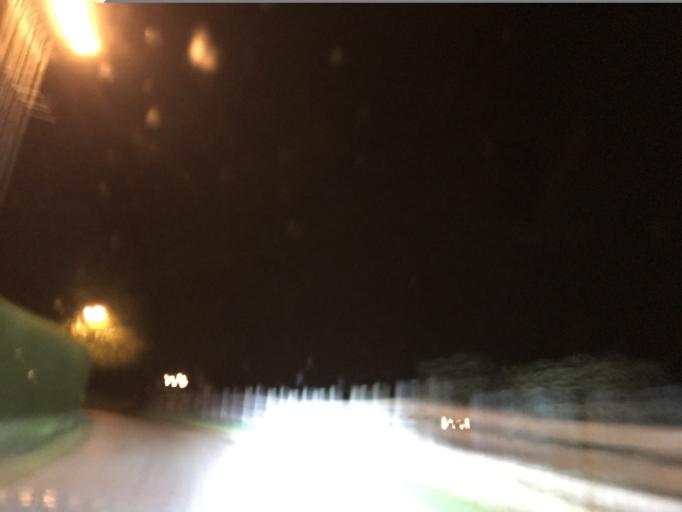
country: FR
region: Auvergne
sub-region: Departement du Puy-de-Dome
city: Celles-sur-Durolle
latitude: 45.8600
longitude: 3.6207
